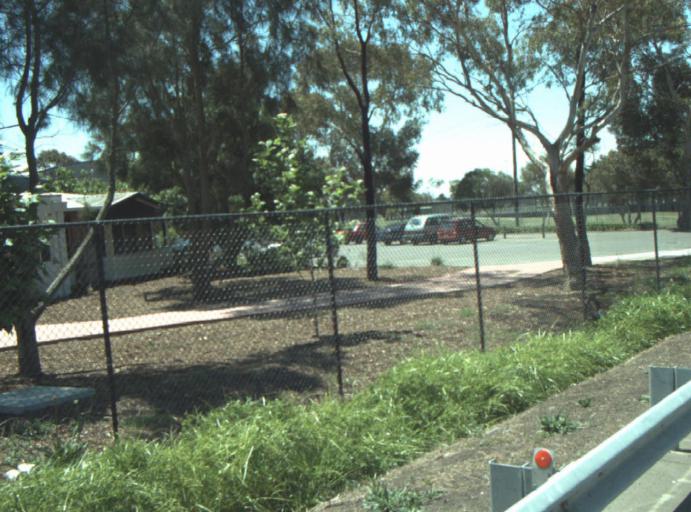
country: AU
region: Victoria
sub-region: Greater Geelong
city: Bell Post Hill
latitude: -38.0973
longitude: 144.3186
